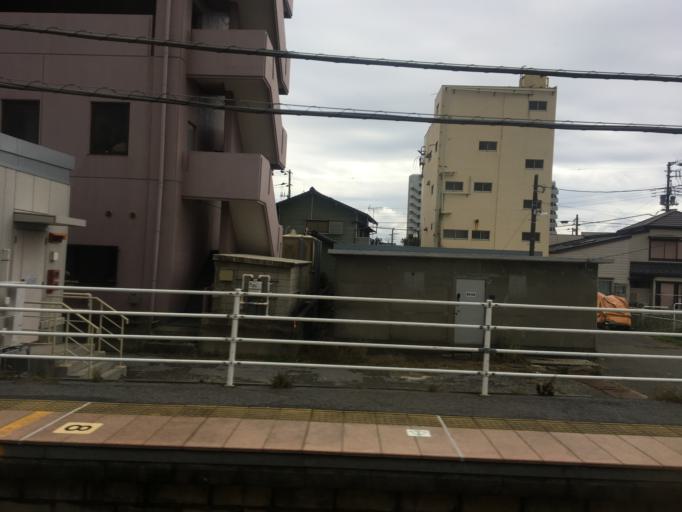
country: JP
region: Chiba
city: Kawaguchi
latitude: 35.1085
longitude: 140.1046
